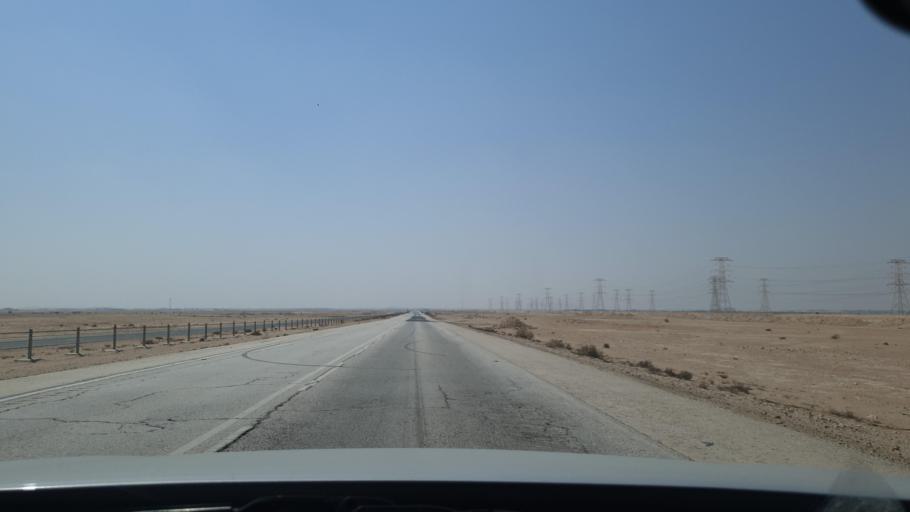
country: QA
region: Al Khawr
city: Al Khawr
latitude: 25.7181
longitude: 51.4509
